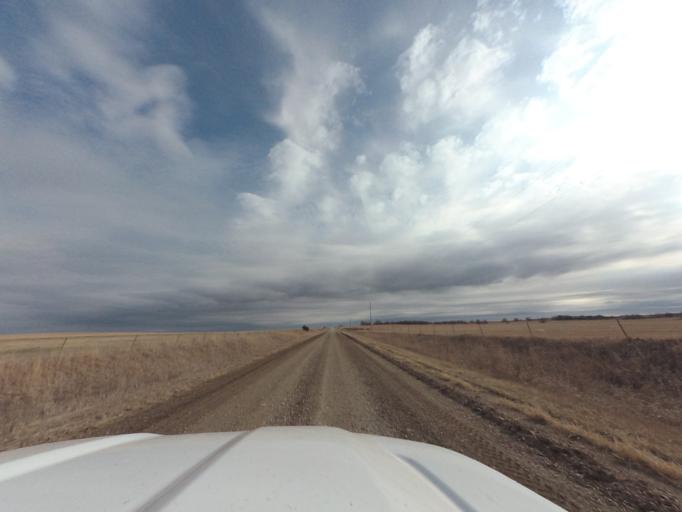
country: US
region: Kansas
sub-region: Chase County
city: Cottonwood Falls
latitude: 38.2169
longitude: -96.6856
